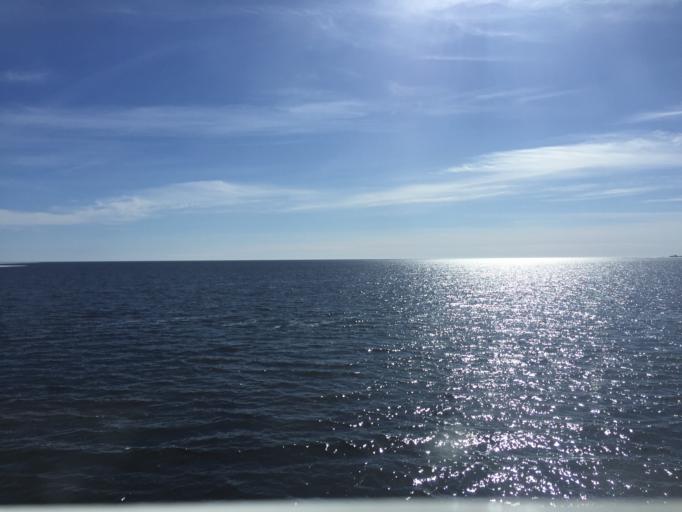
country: EE
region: Laeaene
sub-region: Haapsalu linn
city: Haapsalu
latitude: 58.5760
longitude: 23.4740
